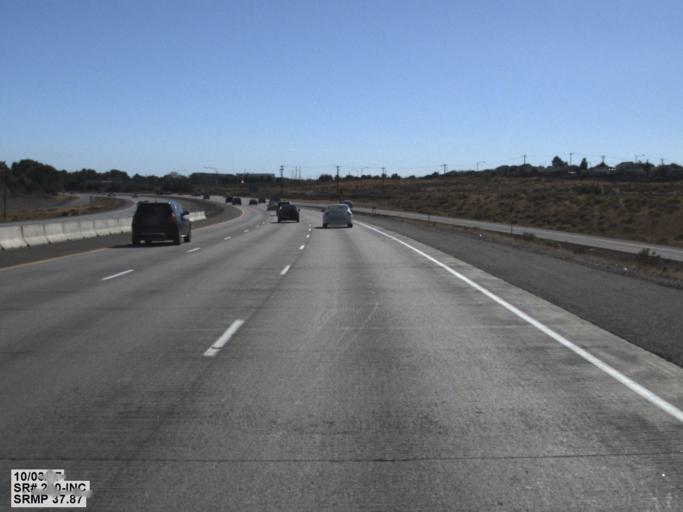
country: US
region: Washington
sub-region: Franklin County
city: West Pasco
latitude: 46.2375
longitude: -119.2425
